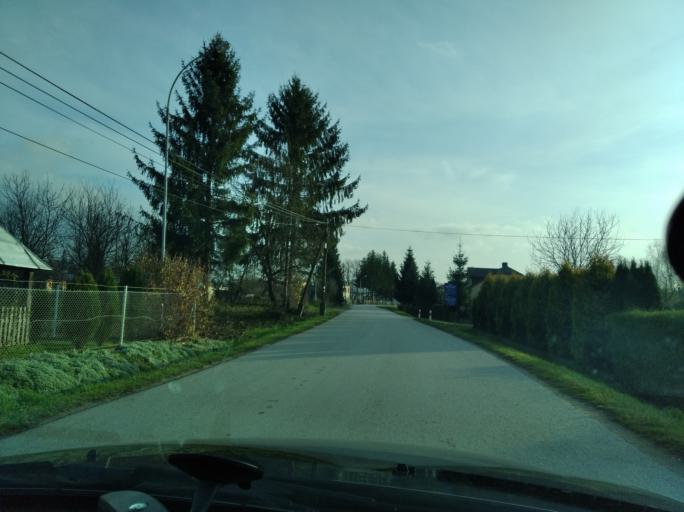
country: PL
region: Subcarpathian Voivodeship
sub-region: Powiat przemyski
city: Przedmiescie Dubieckie
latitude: 49.8351
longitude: 22.3715
